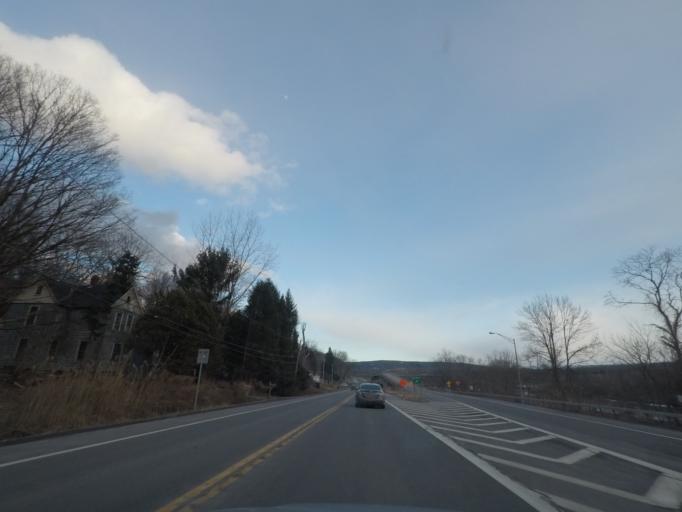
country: US
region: New York
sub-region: Herkimer County
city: Ilion
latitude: 43.0235
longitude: -75.0329
